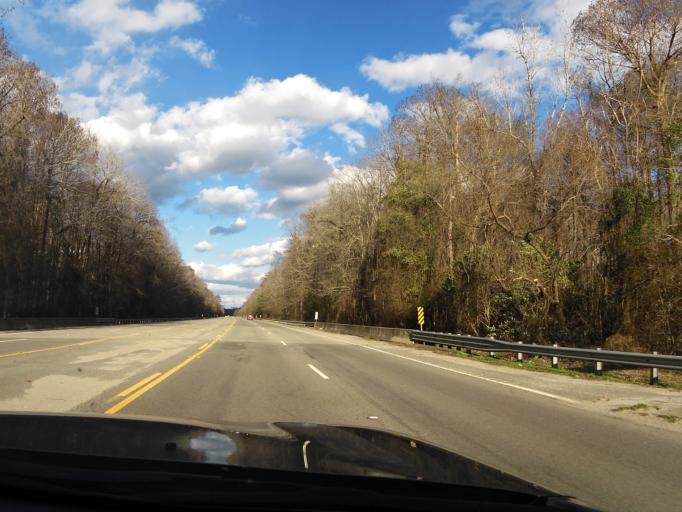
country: US
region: South Carolina
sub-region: Clarendon County
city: Manning
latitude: 33.7089
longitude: -80.2057
